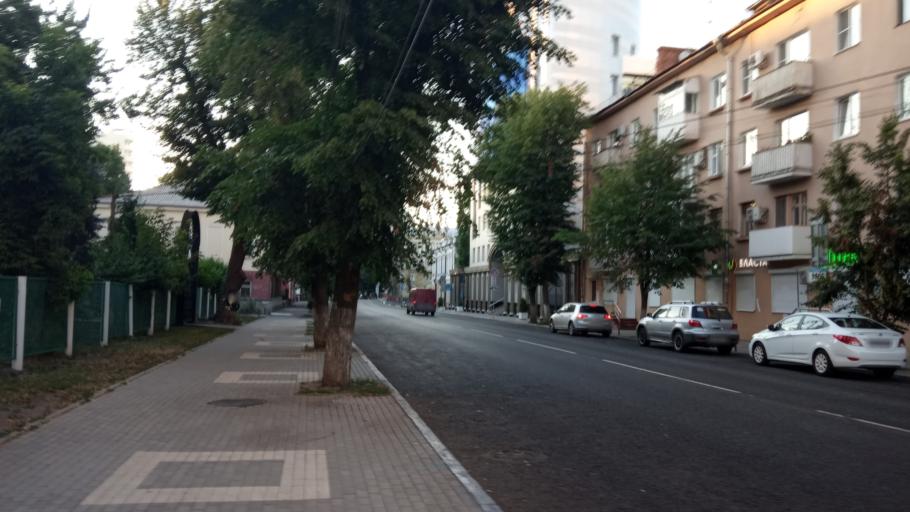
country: RU
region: Voronezj
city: Voronezh
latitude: 51.6601
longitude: 39.2083
